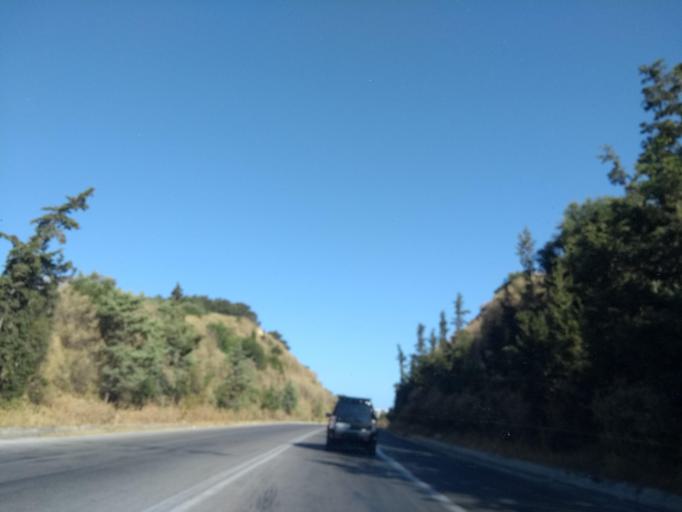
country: GR
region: Crete
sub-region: Nomos Chanias
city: Agia Marina
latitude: 35.5076
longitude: 23.9364
